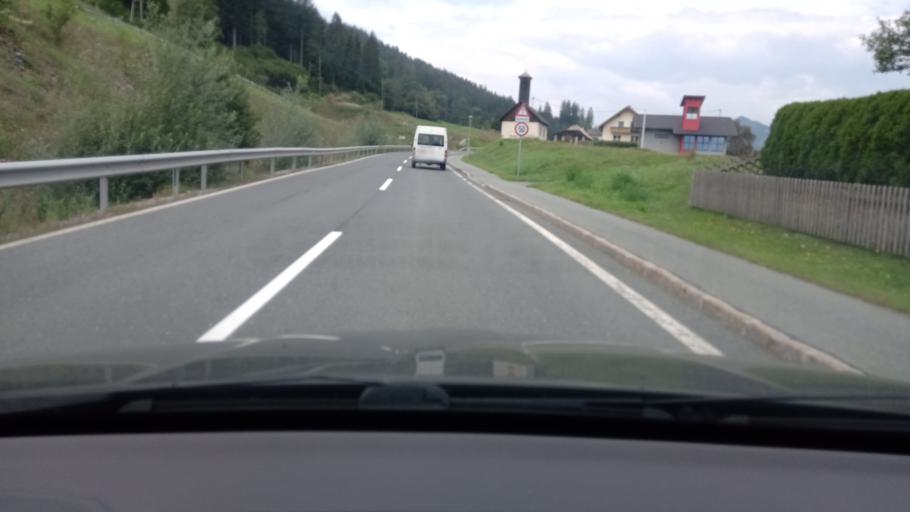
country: AT
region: Carinthia
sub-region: Politischer Bezirk Hermagor
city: Hermagor
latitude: 46.6343
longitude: 13.3507
